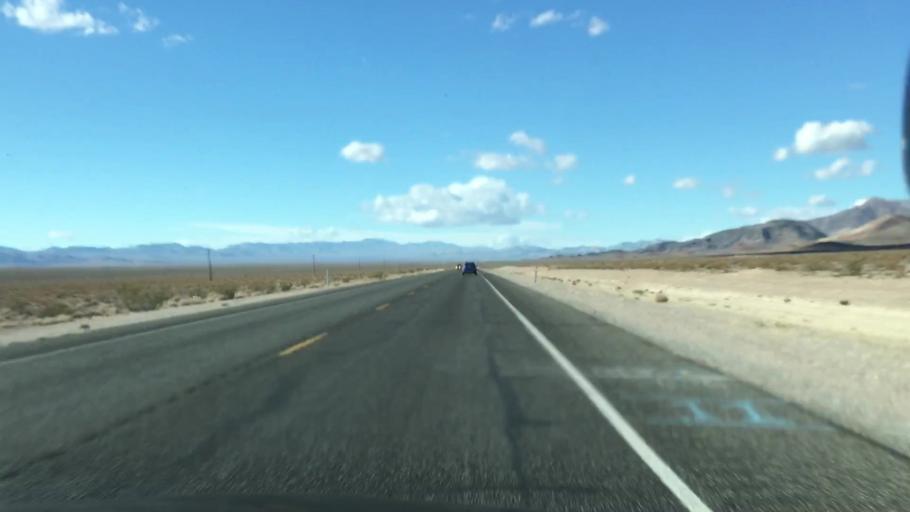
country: US
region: Nevada
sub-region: Nye County
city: Beatty
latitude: 36.6985
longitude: -116.5785
